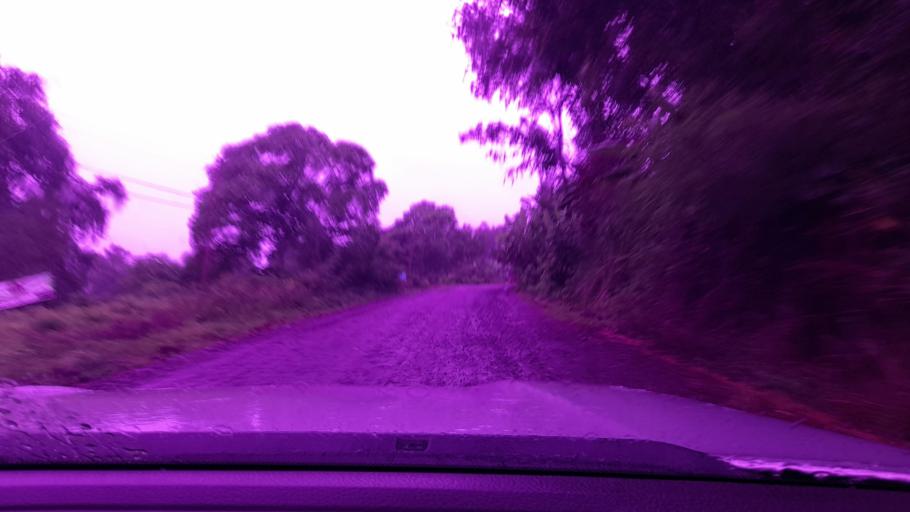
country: ET
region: Oromiya
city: Metu
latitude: 8.3133
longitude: 35.5982
